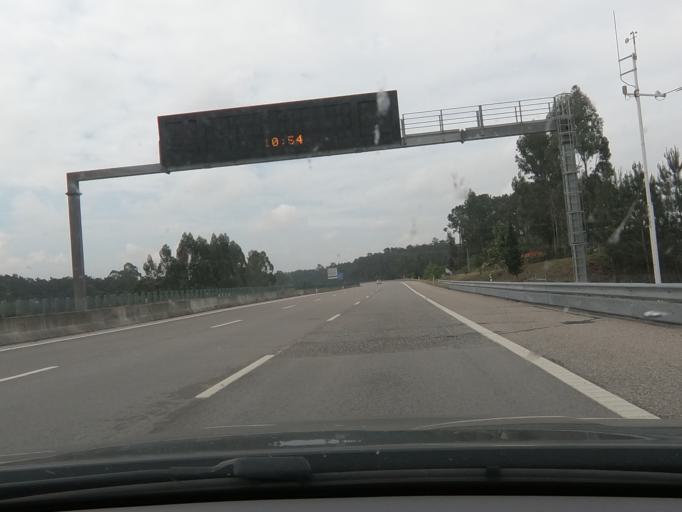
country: PT
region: Leiria
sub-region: Leiria
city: Monte Redondo
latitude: 39.8782
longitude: -8.8202
